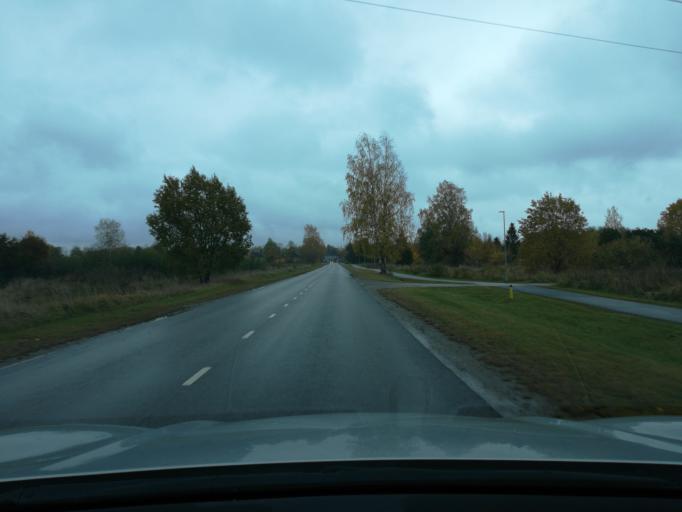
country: EE
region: Ida-Virumaa
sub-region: Johvi vald
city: Johvi
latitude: 59.3149
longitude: 27.4441
